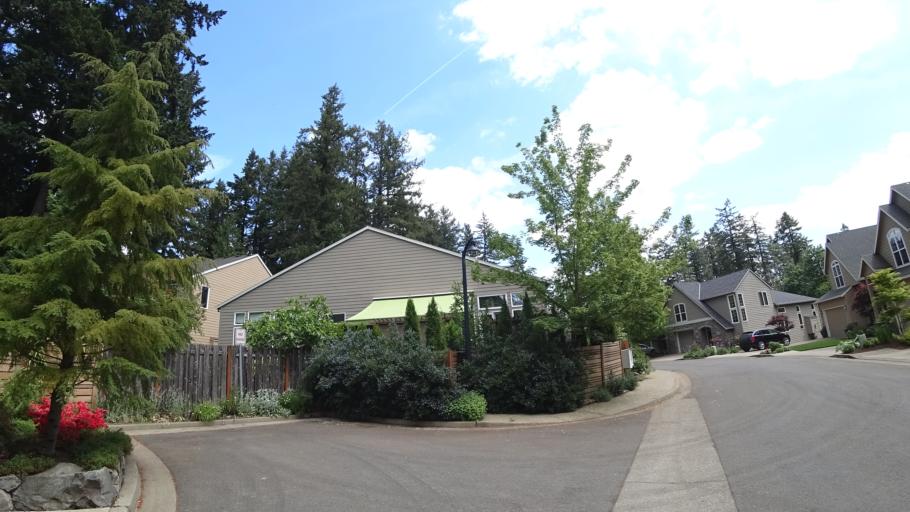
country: US
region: Oregon
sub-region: Washington County
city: King City
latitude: 45.4271
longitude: -122.8052
